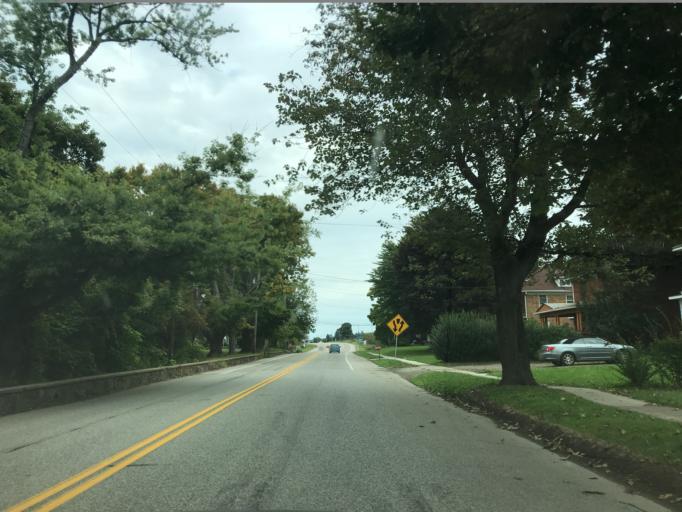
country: US
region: Pennsylvania
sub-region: Erie County
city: North East
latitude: 42.2188
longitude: -79.8247
